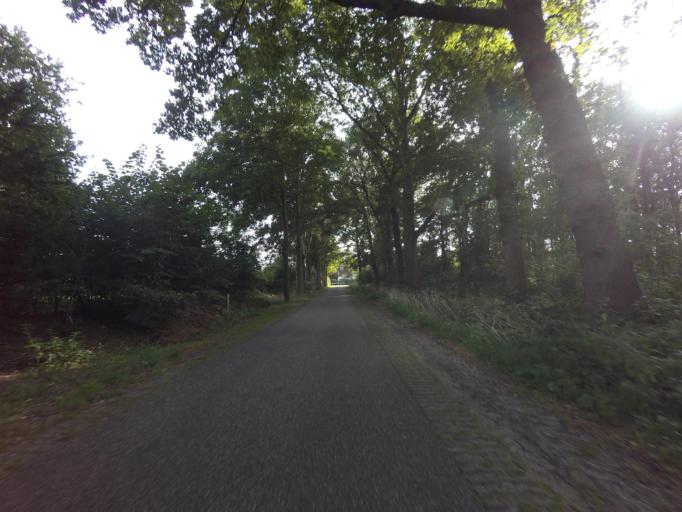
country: DE
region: Lower Saxony
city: Wielen
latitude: 52.5796
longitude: 6.6757
